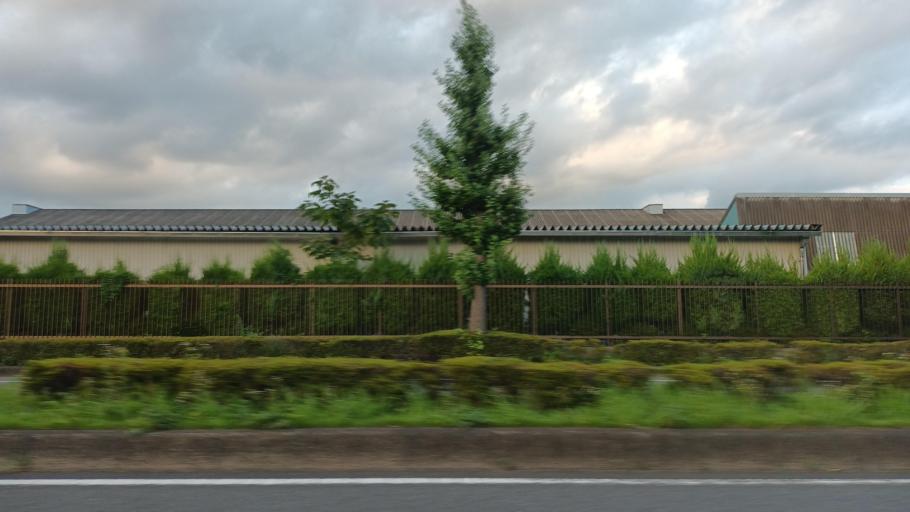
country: JP
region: Tokyo
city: Fussa
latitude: 35.7721
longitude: 139.3152
